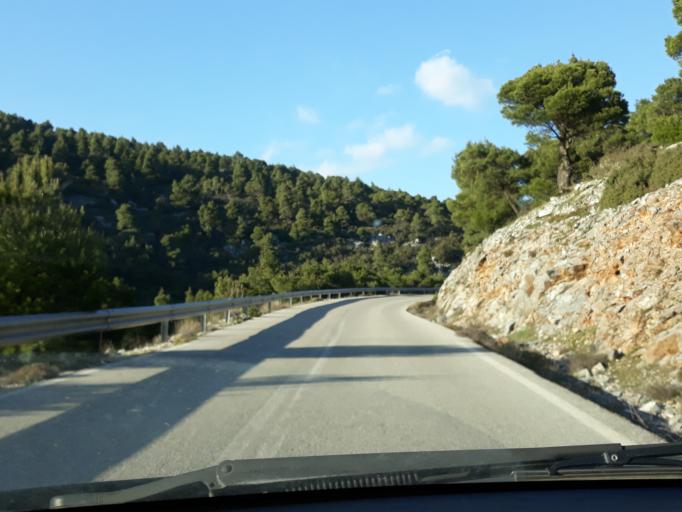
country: GR
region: Attica
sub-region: Nomarchia Dytikis Attikis
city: Fyli
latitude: 38.1533
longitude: 23.6293
